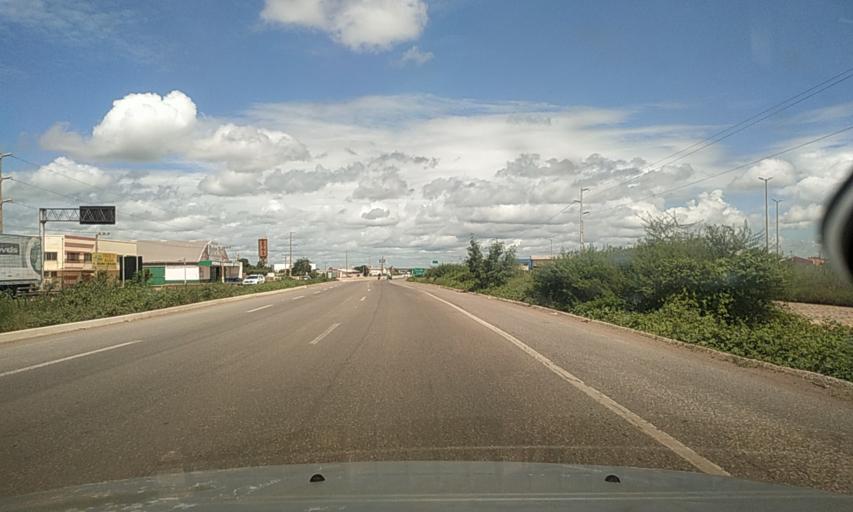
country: BR
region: Rio Grande do Norte
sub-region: Mossoro
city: Mossoro
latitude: -5.1867
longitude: -37.3728
